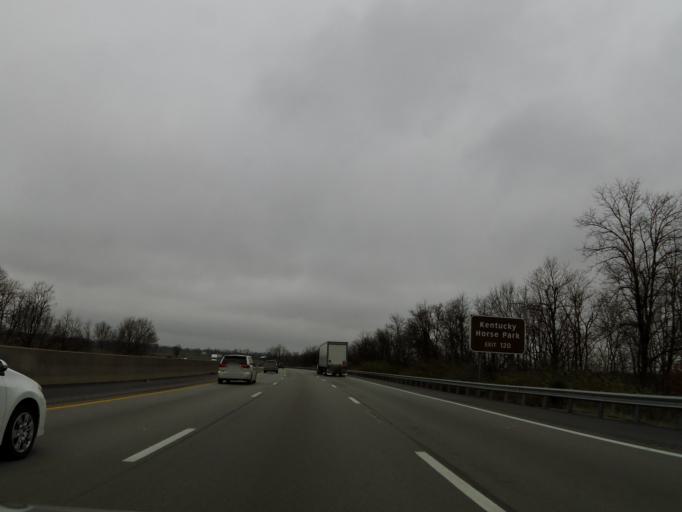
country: US
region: Kentucky
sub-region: Scott County
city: Georgetown
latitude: 38.1726
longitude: -84.5357
